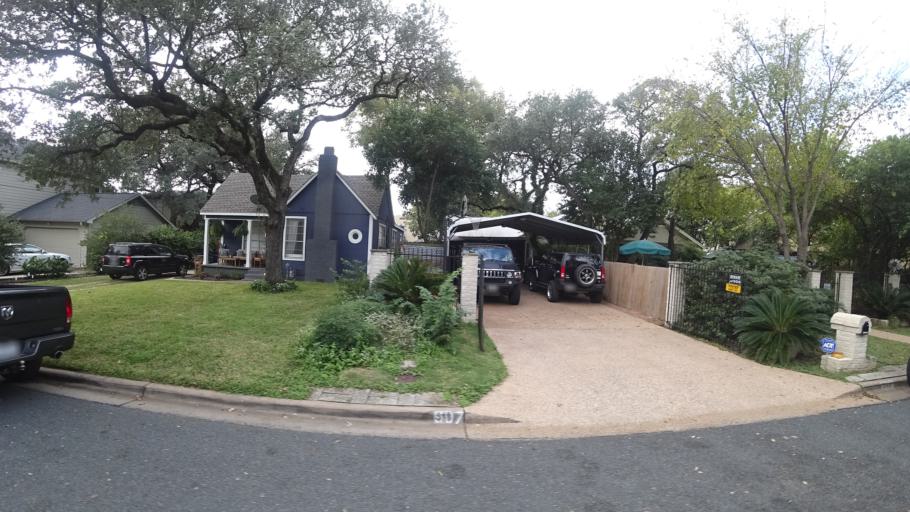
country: US
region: Texas
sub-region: Travis County
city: Austin
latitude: 30.2541
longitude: -97.7574
